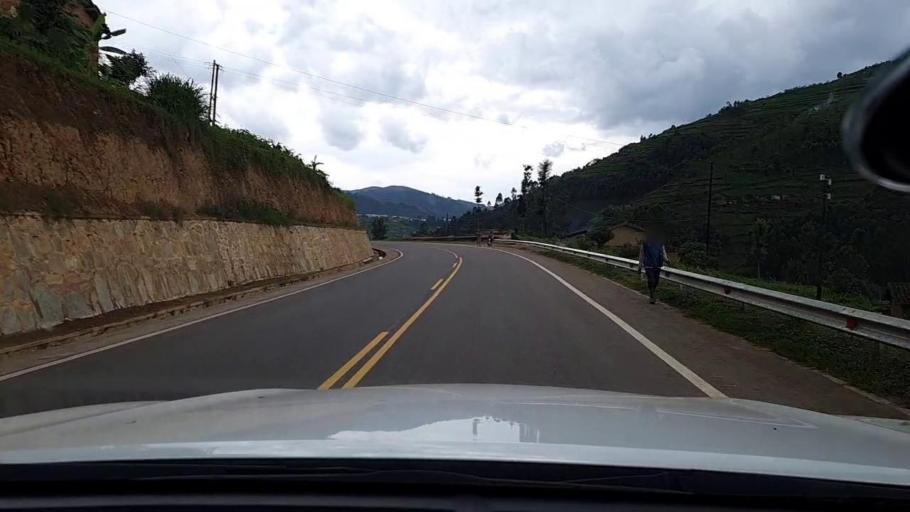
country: RW
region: Northern Province
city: Byumba
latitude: -1.6445
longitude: 29.9247
